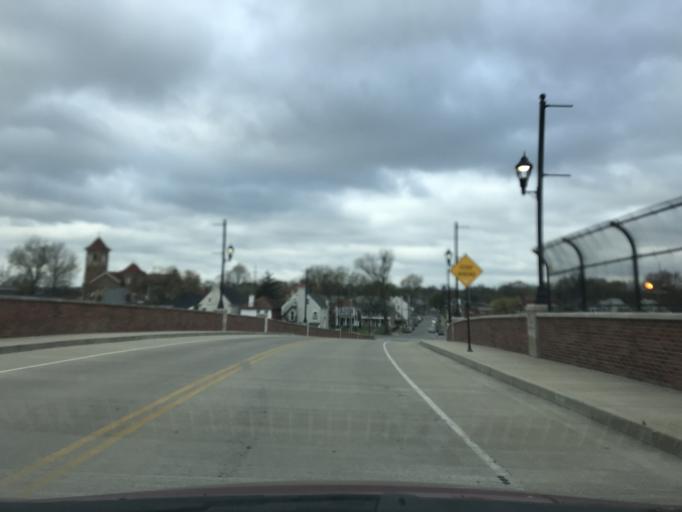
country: US
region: Kentucky
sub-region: Jefferson County
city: Audubon Park
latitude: 38.2074
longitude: -85.7616
